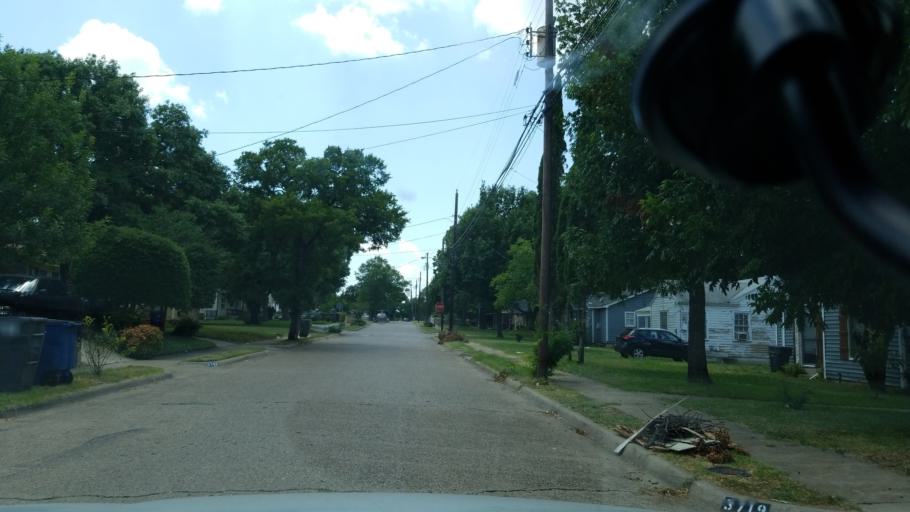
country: US
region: Texas
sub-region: Dallas County
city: Cockrell Hill
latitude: 32.7264
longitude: -96.8813
